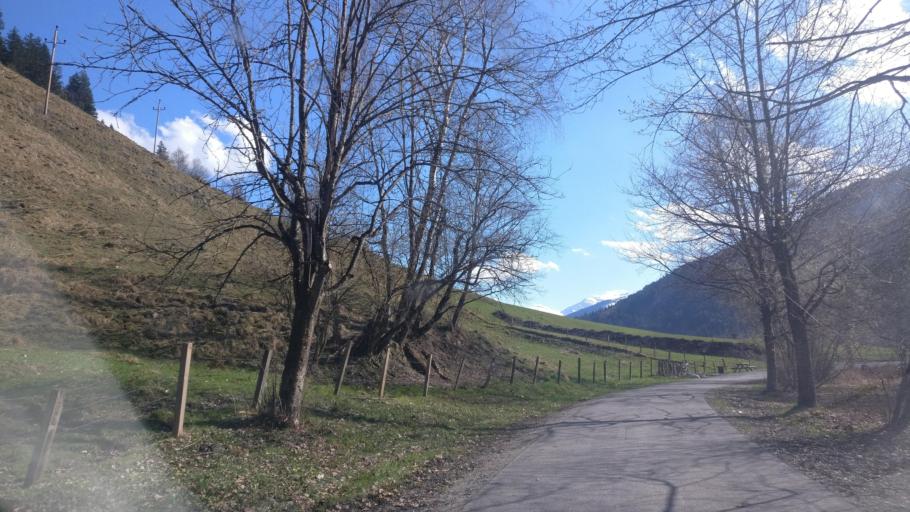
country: AT
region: Salzburg
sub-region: Politischer Bezirk Sankt Johann im Pongau
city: Dorfgastein
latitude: 47.2322
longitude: 13.1098
